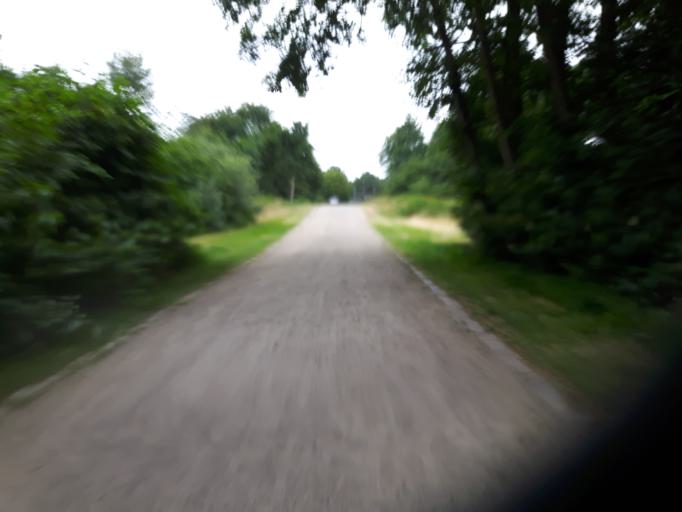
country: DE
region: Lower Saxony
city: Stuhr
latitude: 53.0269
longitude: 8.7393
